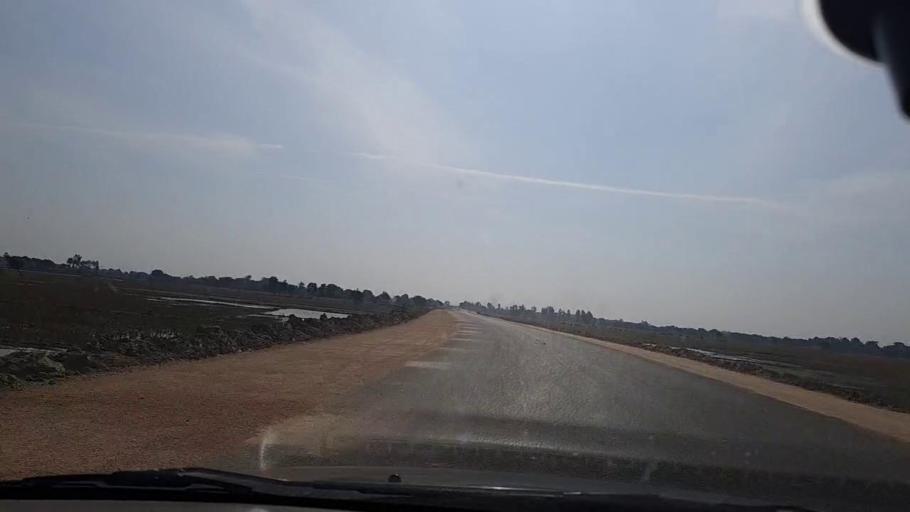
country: PK
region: Sindh
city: Mirpur Batoro
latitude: 24.7417
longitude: 68.2740
